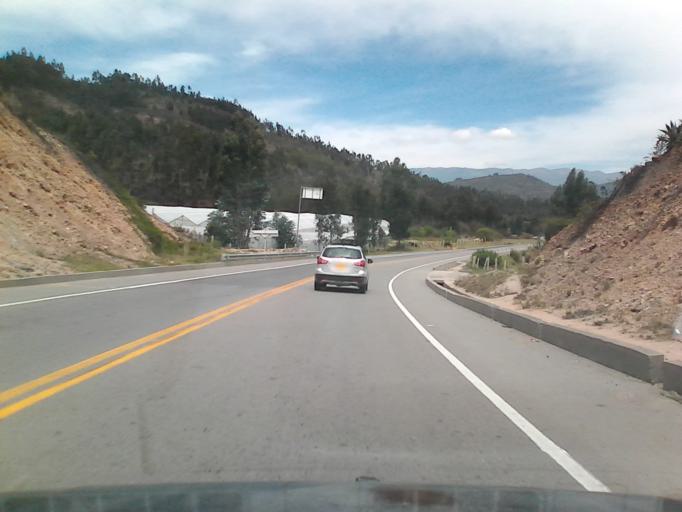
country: CO
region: Boyaca
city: Tibasosa
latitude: 5.7580
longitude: -72.9954
